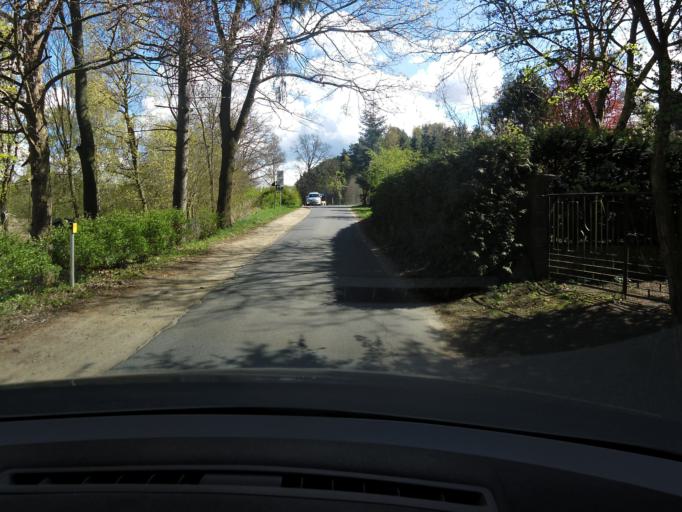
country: DE
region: Mecklenburg-Vorpommern
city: Malchow
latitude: 53.4662
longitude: 12.3476
